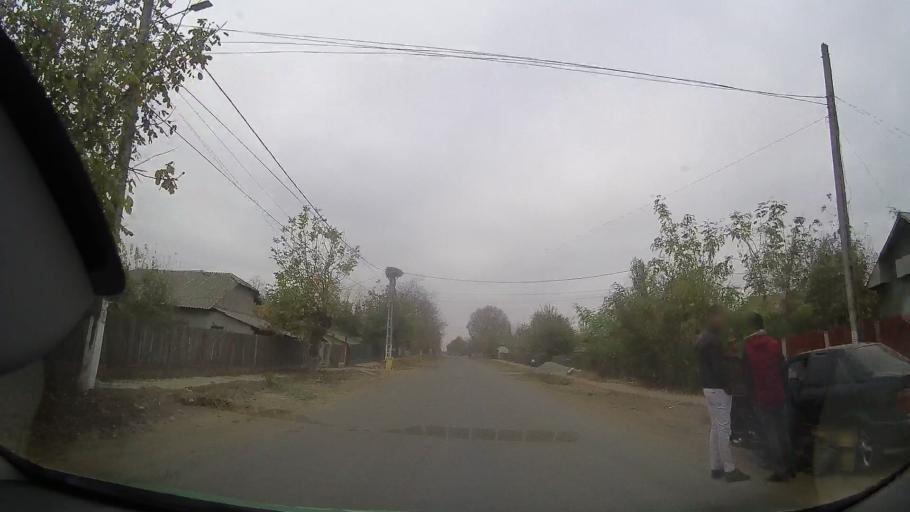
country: RO
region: Buzau
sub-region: Comuna Luciu
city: Luciu
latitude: 44.9690
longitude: 27.0882
